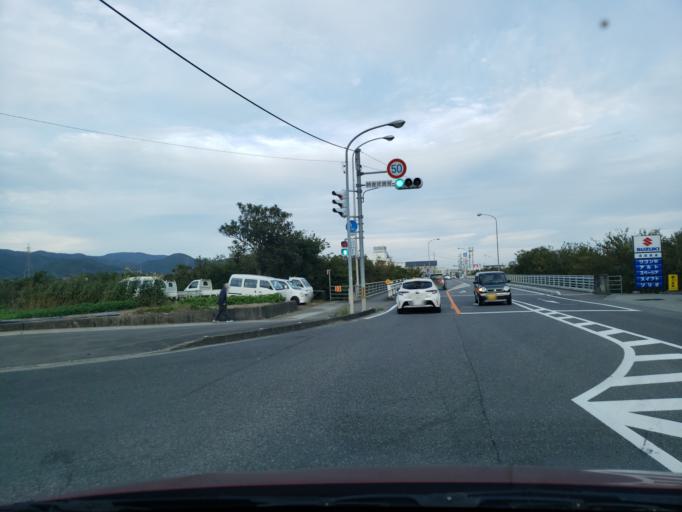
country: JP
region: Tokushima
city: Kamojimacho-jogejima
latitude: 34.0829
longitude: 134.2720
